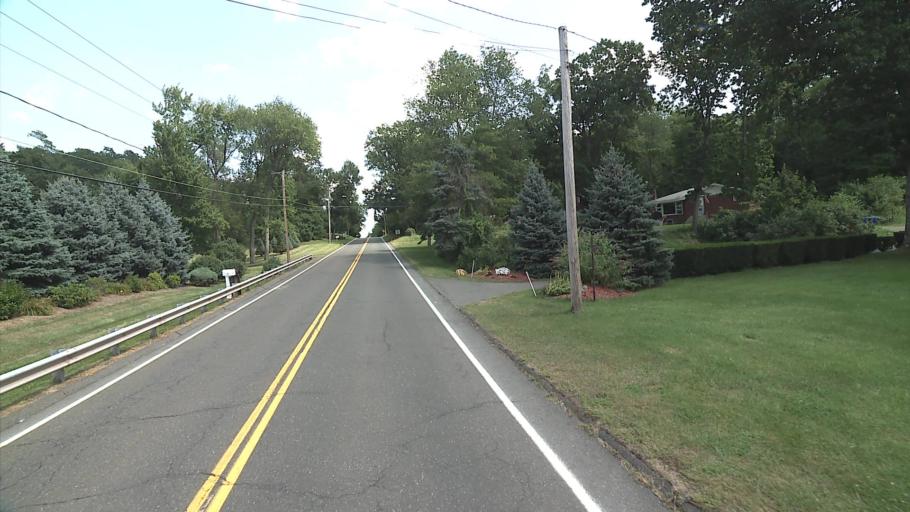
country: US
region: Connecticut
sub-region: Hartford County
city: Windsor Locks
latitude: 41.8932
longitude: -72.6056
